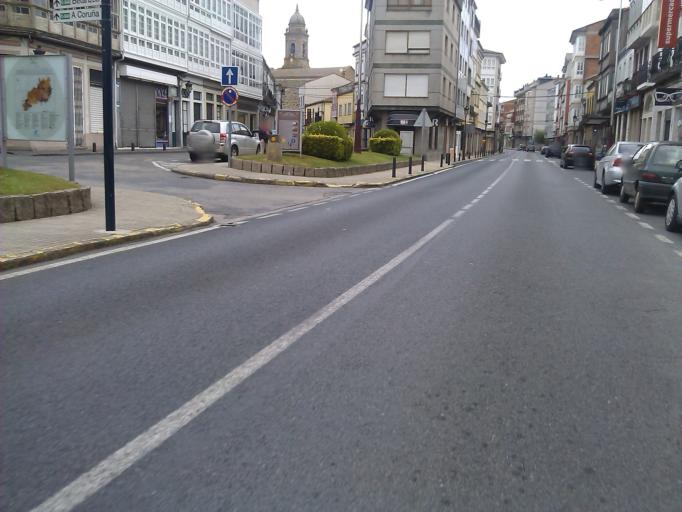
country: ES
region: Galicia
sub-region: Provincia da Coruna
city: Melide
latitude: 42.9144
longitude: -8.0149
